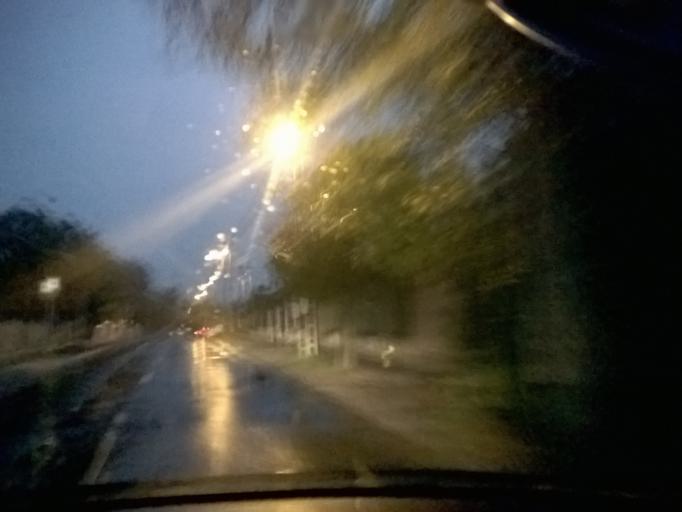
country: HU
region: Budapest
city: Budapest XXI. keruelet
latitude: 47.4099
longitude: 19.0723
